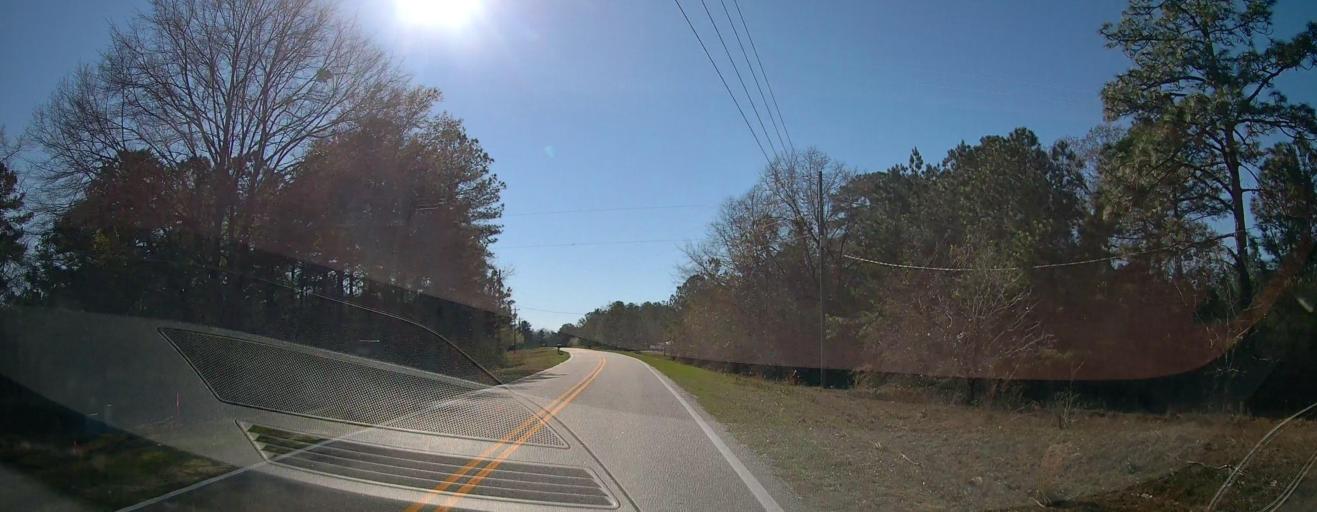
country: US
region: Georgia
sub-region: Peach County
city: Byron
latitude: 32.6927
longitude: -83.7884
